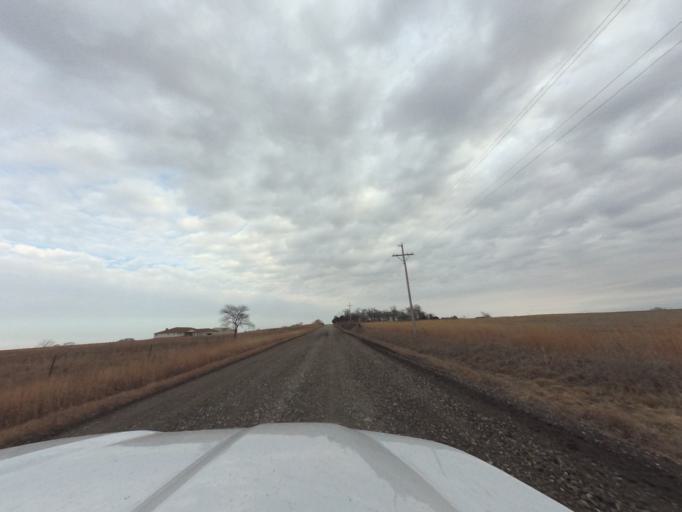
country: US
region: Kansas
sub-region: Chase County
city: Cottonwood Falls
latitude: 38.4453
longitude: -96.3731
